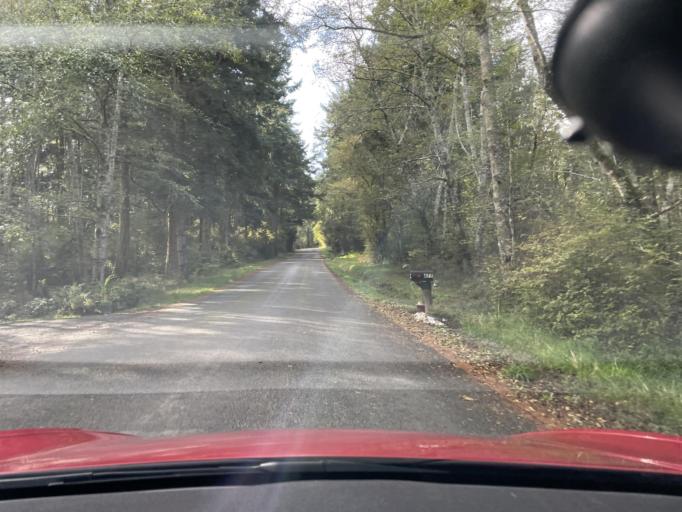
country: US
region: Washington
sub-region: San Juan County
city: Friday Harbor
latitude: 48.4818
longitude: -123.0419
